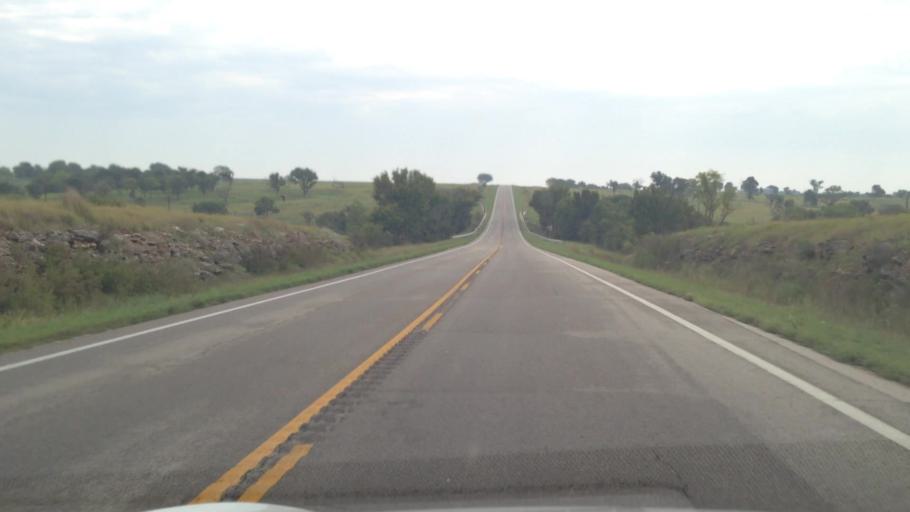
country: US
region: Kansas
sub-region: Bourbon County
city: Fort Scott
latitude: 37.8872
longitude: -95.0281
